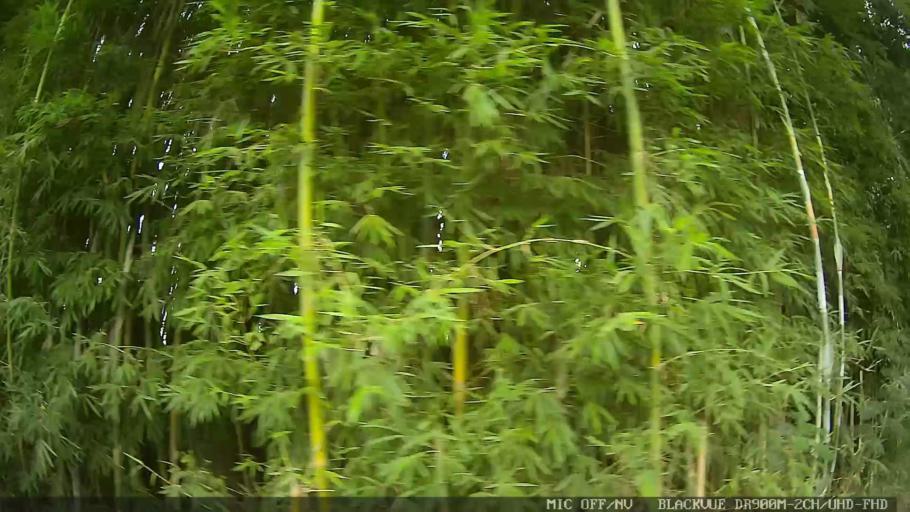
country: BR
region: Sao Paulo
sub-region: Atibaia
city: Atibaia
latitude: -23.1282
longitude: -46.6027
